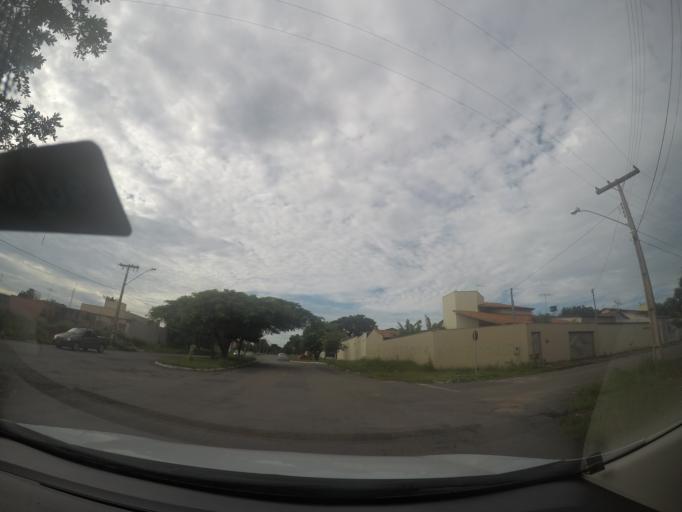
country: BR
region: Goias
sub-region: Goiania
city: Goiania
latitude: -16.6803
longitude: -49.2024
